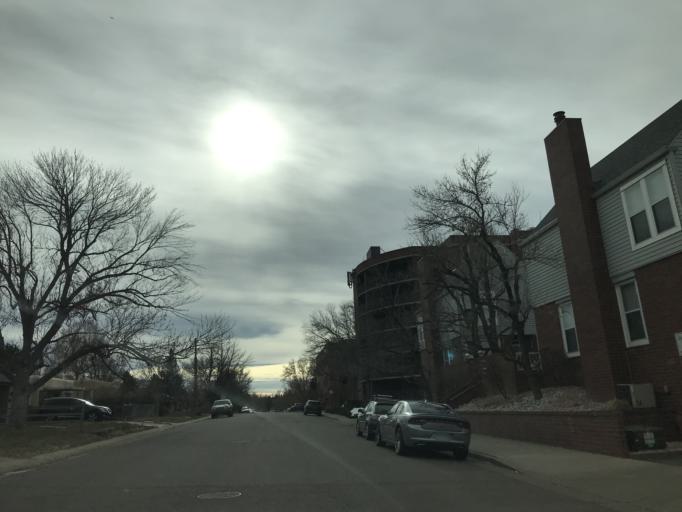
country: US
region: Colorado
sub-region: Arapahoe County
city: Glendale
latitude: 39.7325
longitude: -104.9184
